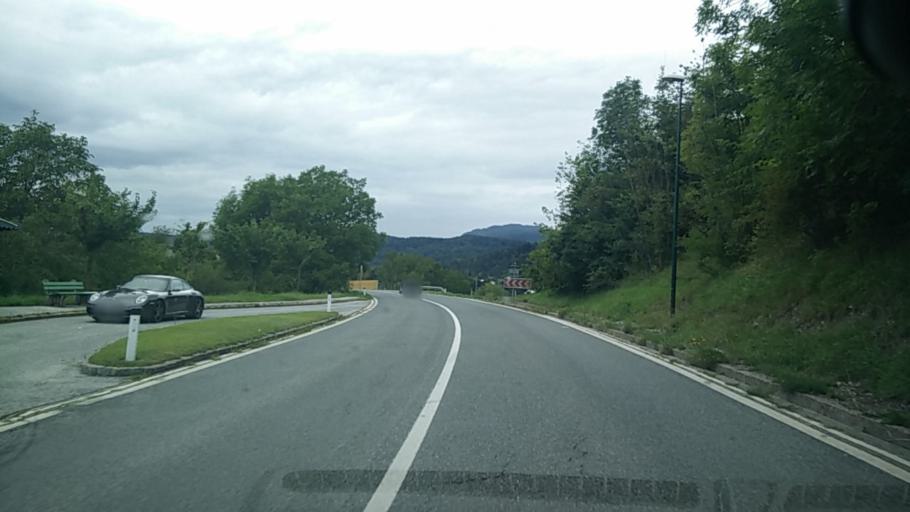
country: AT
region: Carinthia
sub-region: Politischer Bezirk Klagenfurt Land
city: Maria Worth
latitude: 46.6313
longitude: 14.1639
